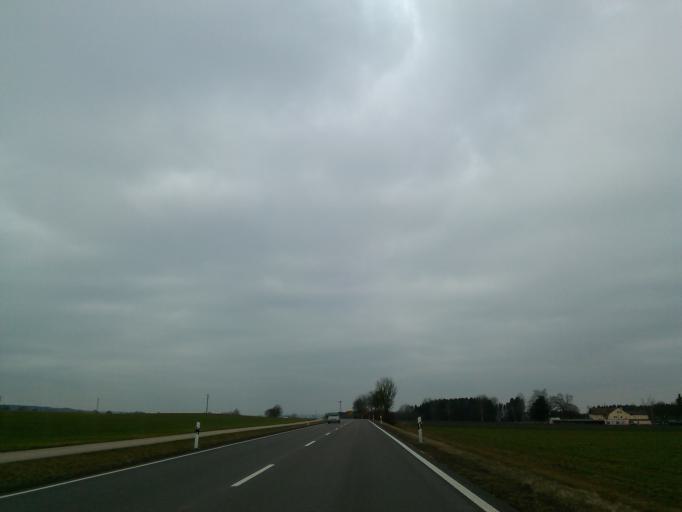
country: DE
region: Bavaria
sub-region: Swabia
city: Kutzenhausen
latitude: 48.3234
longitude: 10.6837
